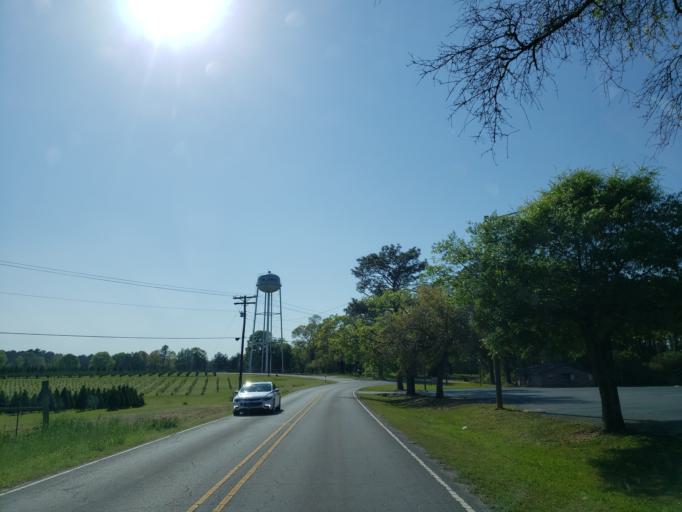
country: US
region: Mississippi
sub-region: Forrest County
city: Rawls Springs
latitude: 31.4925
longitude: -89.3525
